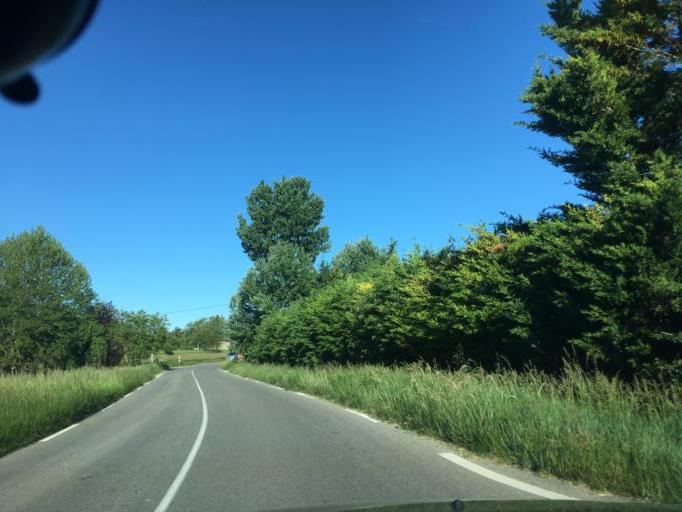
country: FR
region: Provence-Alpes-Cote d'Azur
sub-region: Departement du Var
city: Rians
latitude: 43.6133
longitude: 5.7495
